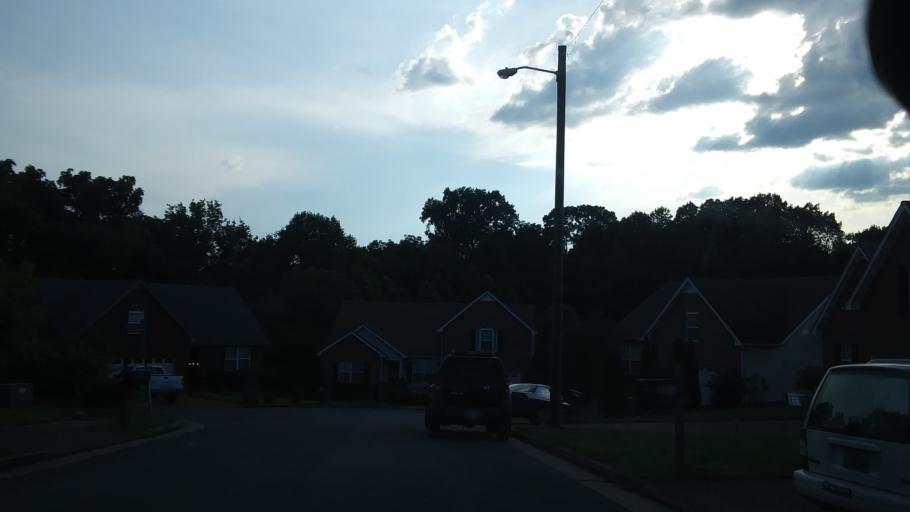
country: US
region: Tennessee
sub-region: Rutherford County
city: La Vergne
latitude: 36.0891
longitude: -86.6593
